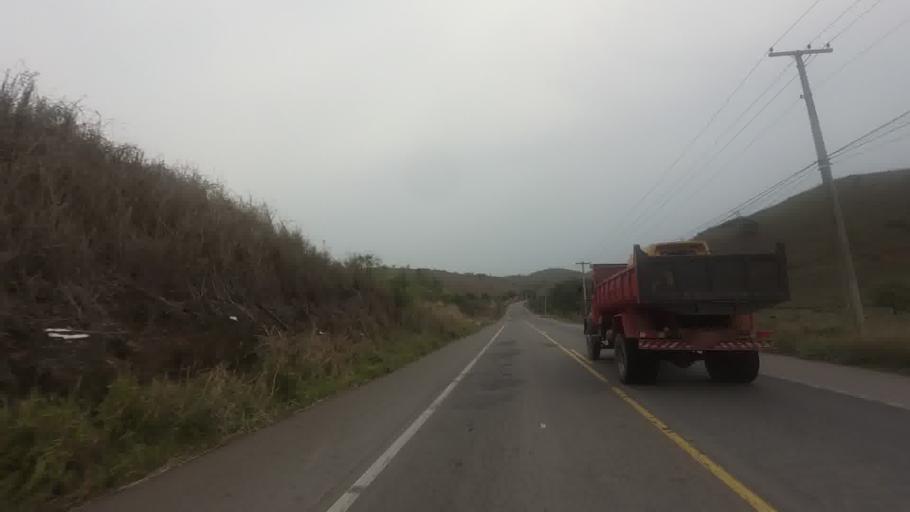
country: BR
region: Rio de Janeiro
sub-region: Santo Antonio De Padua
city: Santo Antonio de Padua
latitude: -21.5988
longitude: -42.2313
